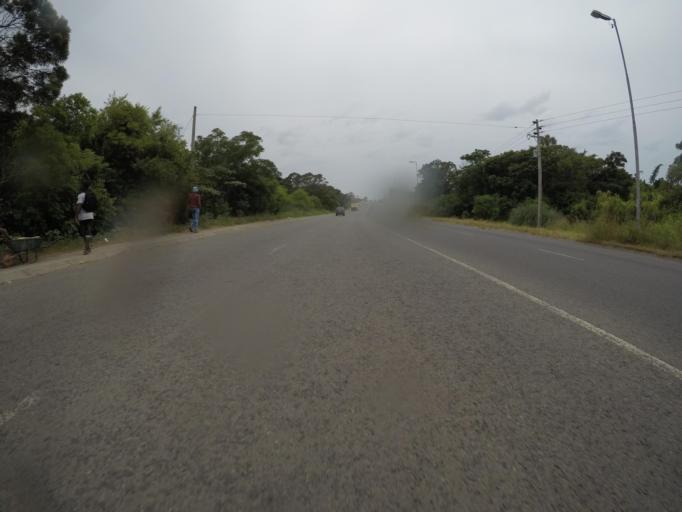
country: ZA
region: Eastern Cape
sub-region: Buffalo City Metropolitan Municipality
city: East London
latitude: -32.9988
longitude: 27.8438
